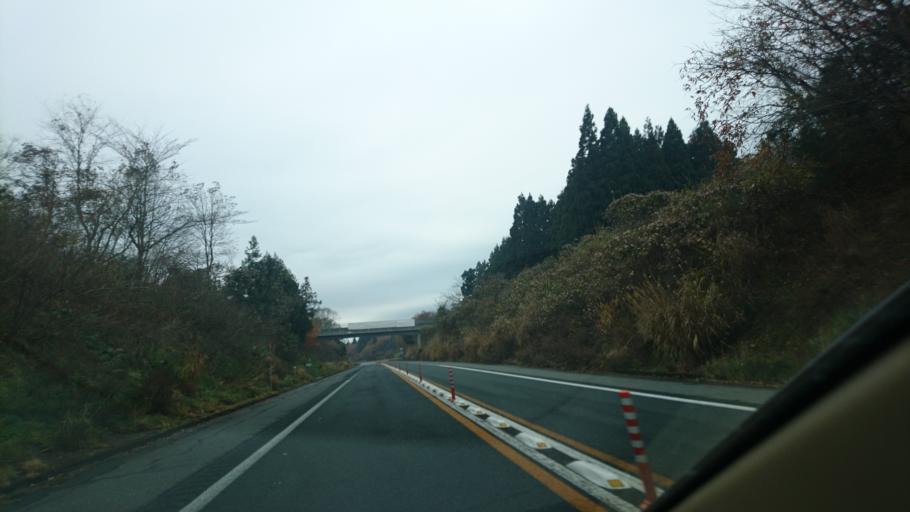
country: JP
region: Iwate
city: Kitakami
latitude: 39.2804
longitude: 141.0143
